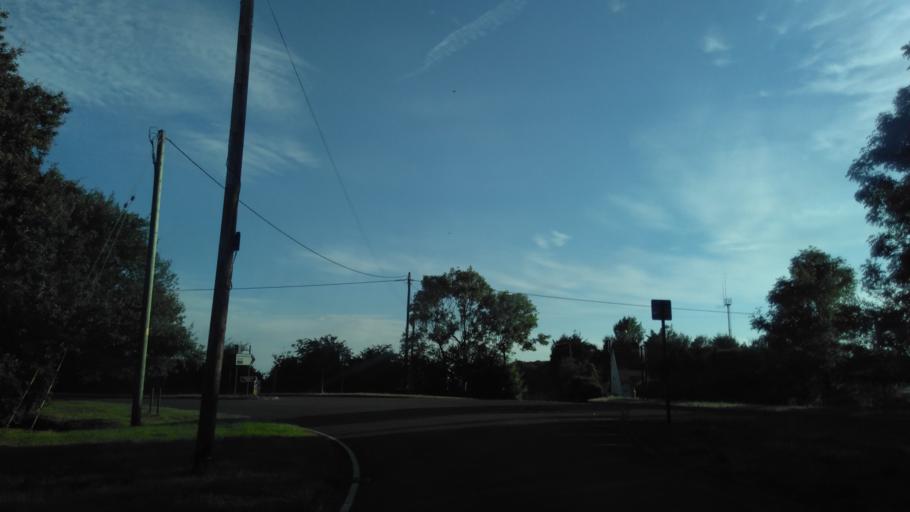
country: GB
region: England
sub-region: Kent
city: Dunkirk
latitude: 51.2909
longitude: 0.9816
